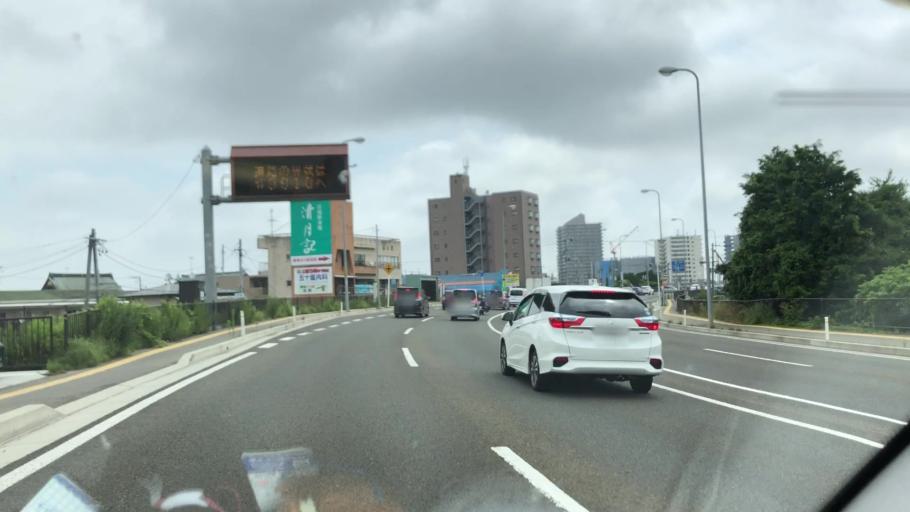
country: JP
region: Miyagi
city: Rifu
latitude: 38.2717
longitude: 140.9582
